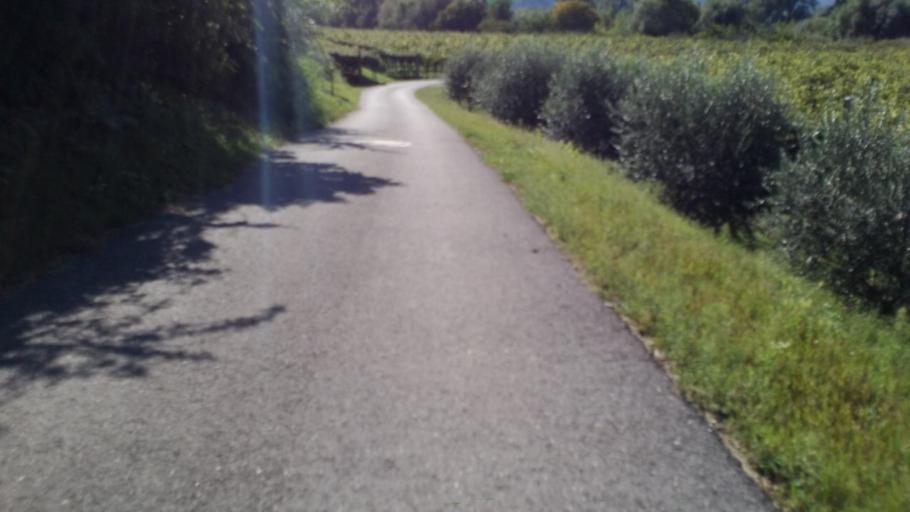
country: IT
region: Veneto
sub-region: Provincia di Verona
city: Rivalta
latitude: 45.6696
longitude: 10.9017
